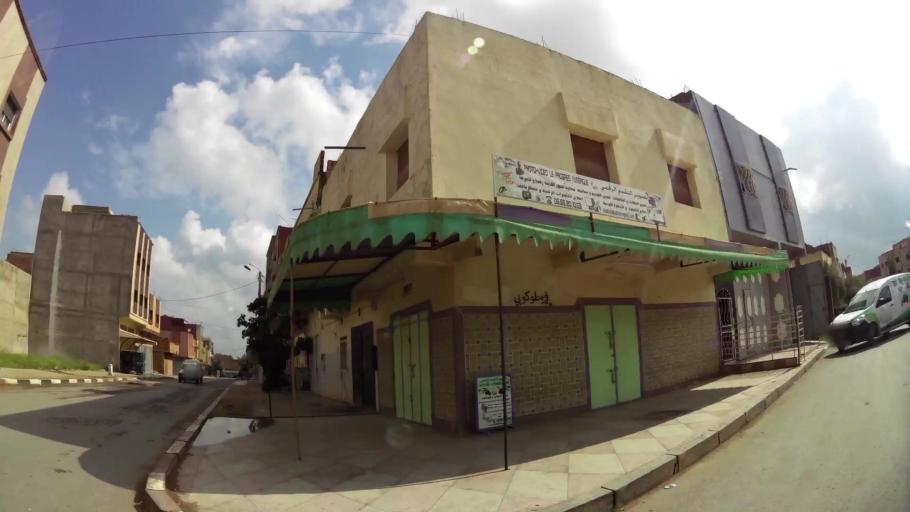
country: MA
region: Rabat-Sale-Zemmour-Zaer
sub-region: Khemisset
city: Tiflet
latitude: 33.8955
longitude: -6.3215
